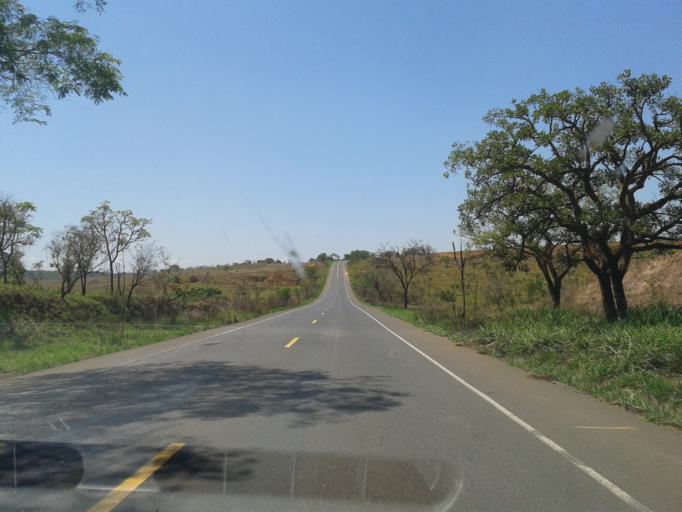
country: BR
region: Minas Gerais
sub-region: Araxa
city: Araxa
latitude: -19.4752
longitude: -47.1525
